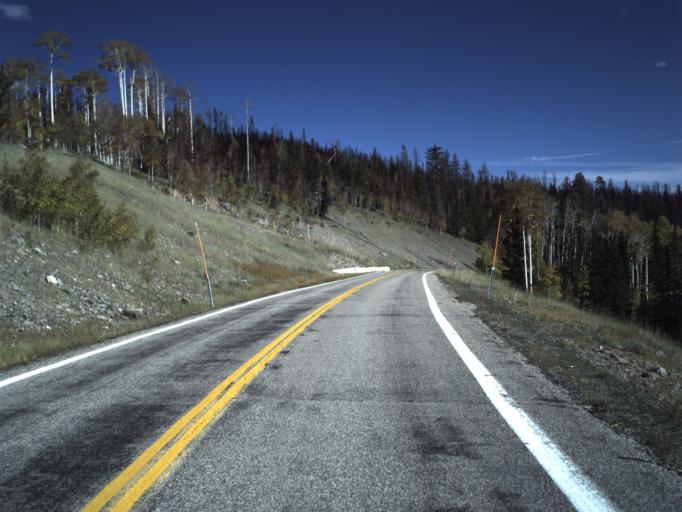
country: US
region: Utah
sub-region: Iron County
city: Parowan
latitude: 37.6642
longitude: -112.7197
